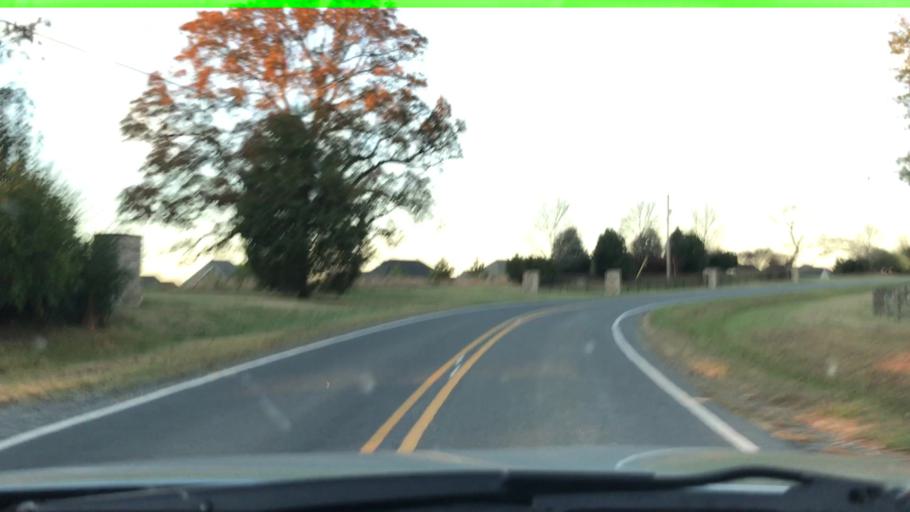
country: US
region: North Carolina
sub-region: Union County
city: Wesley Chapel
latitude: 34.9876
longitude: -80.7206
